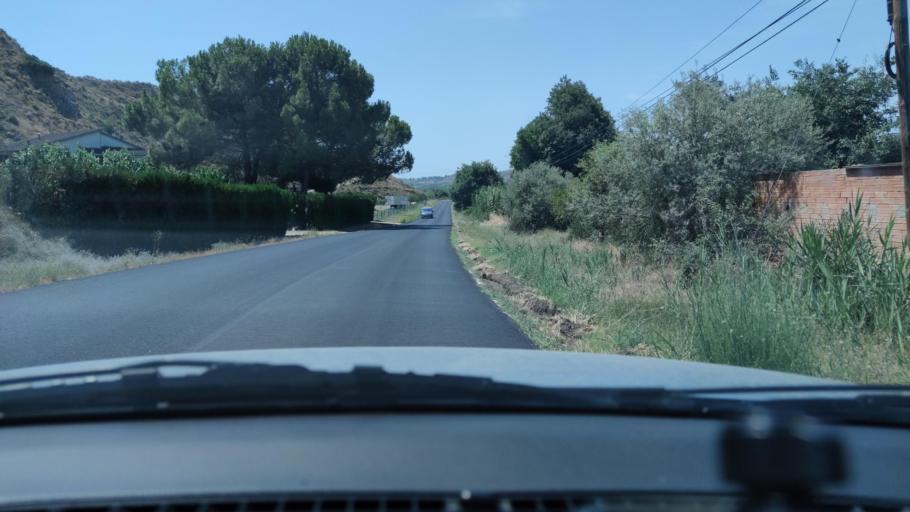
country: ES
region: Catalonia
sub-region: Provincia de Lleida
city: Alfarras
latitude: 41.8337
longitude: 0.5818
